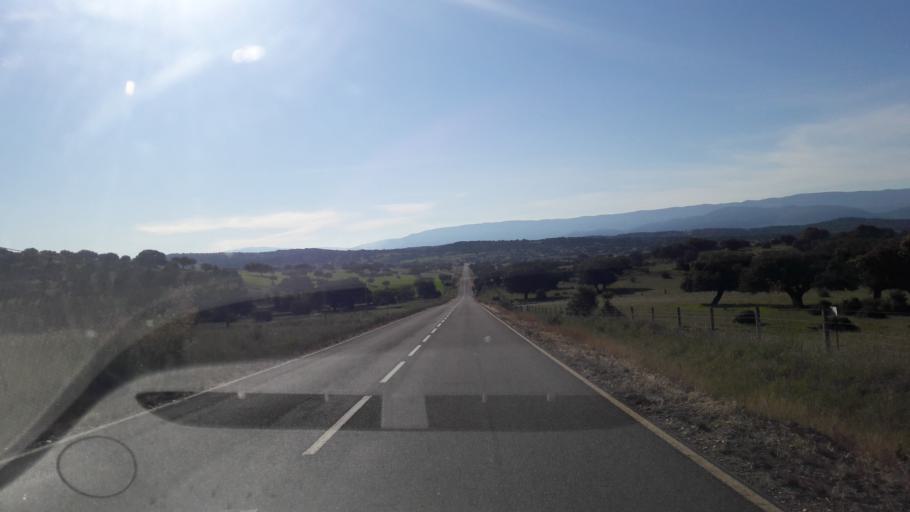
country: ES
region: Castille and Leon
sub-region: Provincia de Salamanca
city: Puente del Congosto
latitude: 40.5291
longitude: -5.5176
